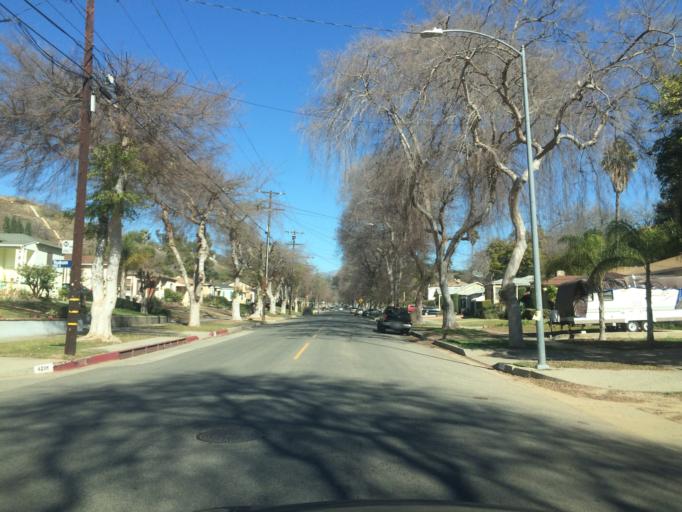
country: US
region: California
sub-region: Los Angeles County
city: South Pasadena
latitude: 34.0944
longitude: -118.1811
